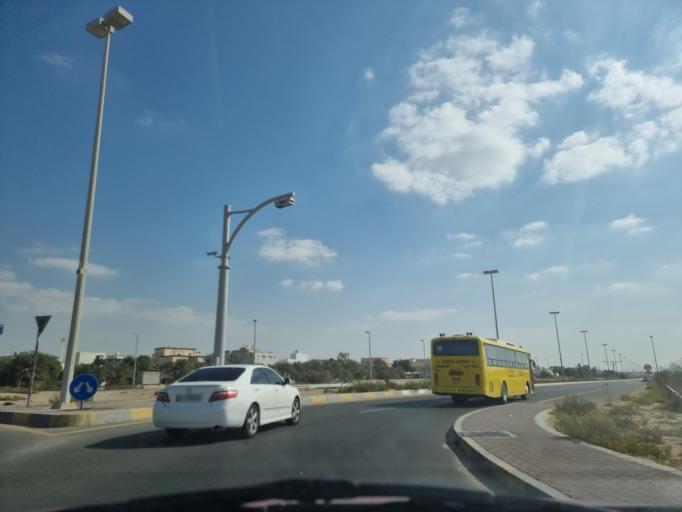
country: AE
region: Abu Dhabi
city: Abu Dhabi
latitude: 24.4128
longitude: 54.7327
